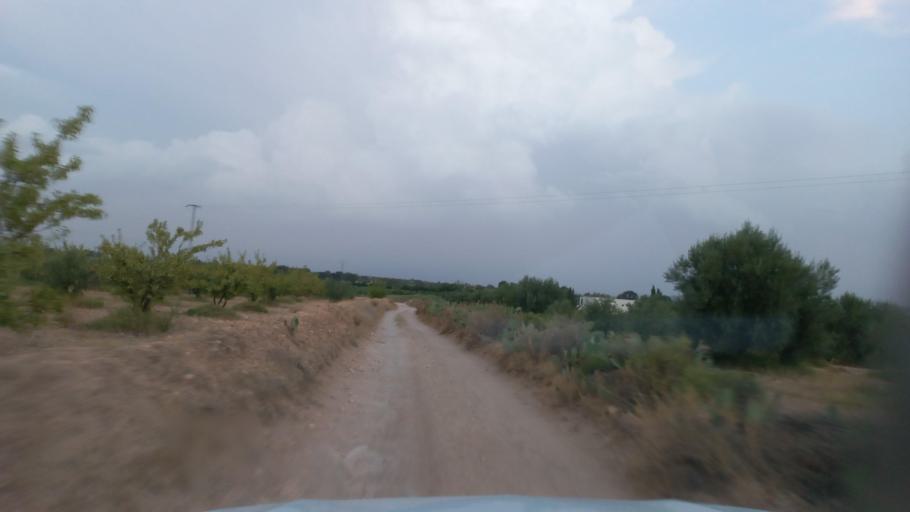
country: TN
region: Al Qasrayn
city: Kasserine
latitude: 35.2674
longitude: 9.0366
